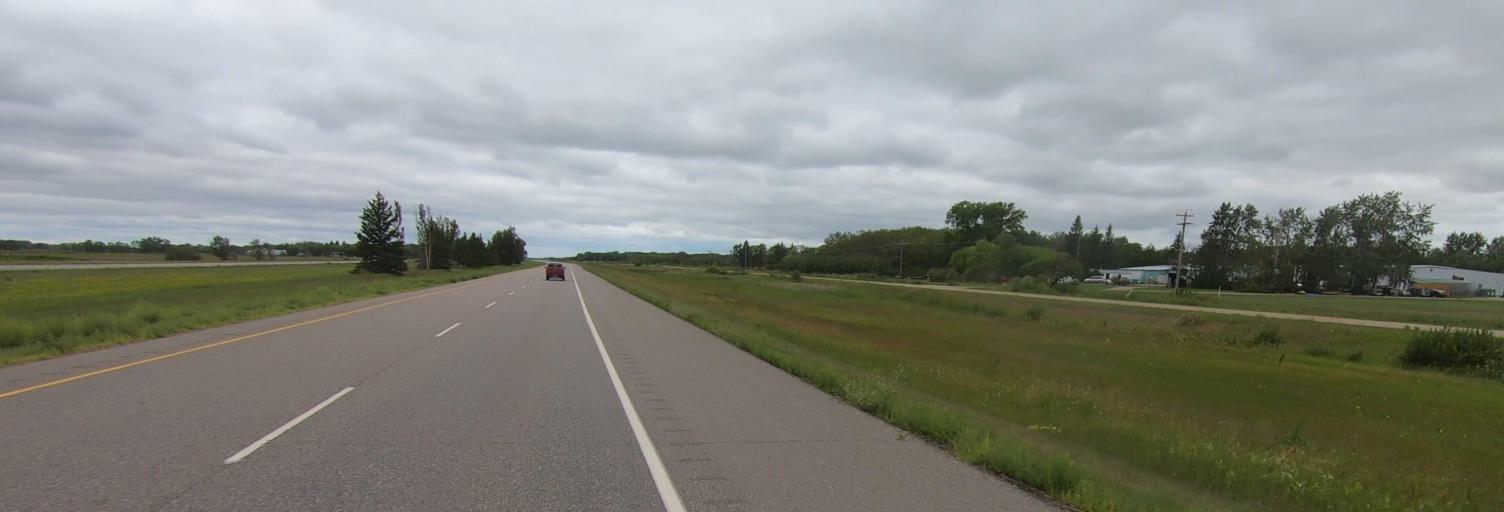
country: CA
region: Manitoba
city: Portage la Prairie
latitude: 49.9753
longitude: -98.6599
